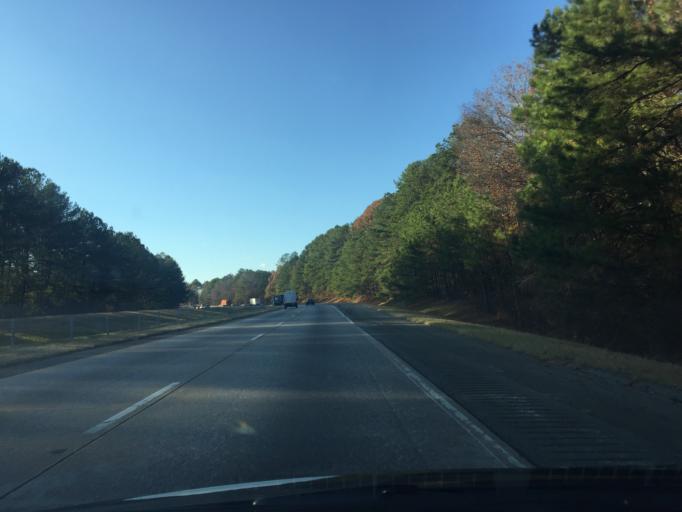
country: US
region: Georgia
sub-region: Bibb County
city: Macon
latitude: 32.9389
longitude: -83.7510
